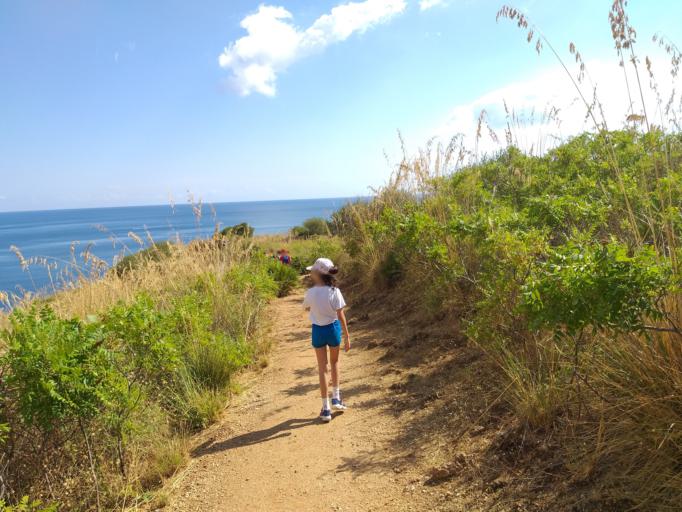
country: IT
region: Sicily
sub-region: Trapani
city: Castelluzzo
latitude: 38.0863
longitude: 12.8062
